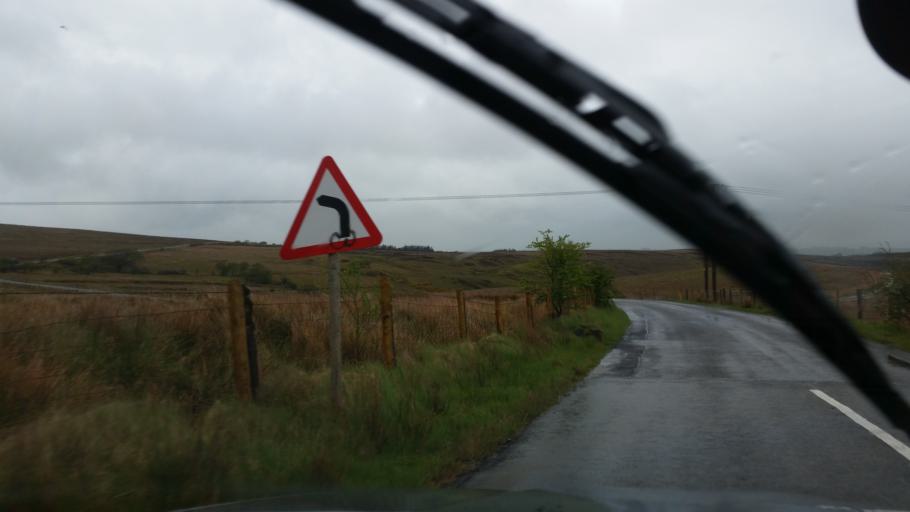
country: GB
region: Northern Ireland
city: Fintona
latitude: 54.4419
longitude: -7.3249
